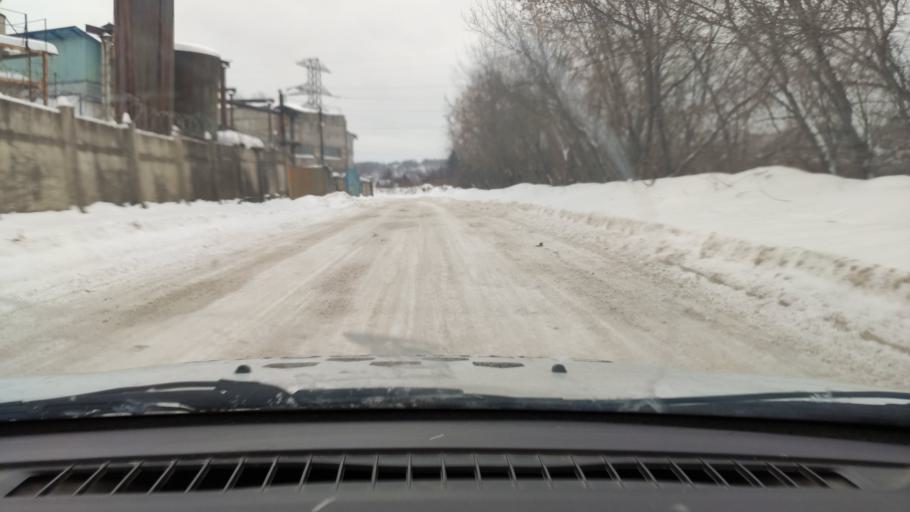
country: RU
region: Perm
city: Kungur
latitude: 57.4477
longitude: 56.9236
